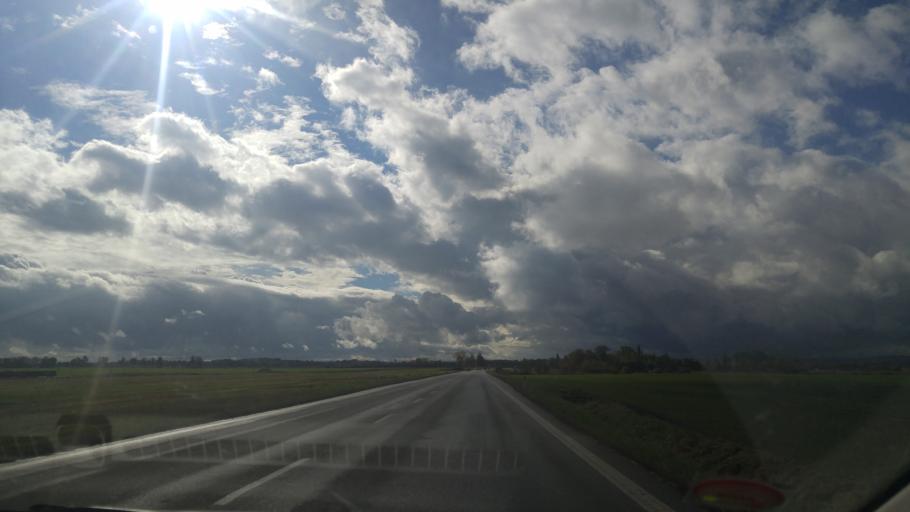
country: CZ
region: Jihocesky
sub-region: Okres Tabor
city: Veseli nad Luznici
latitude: 49.1789
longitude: 14.6907
